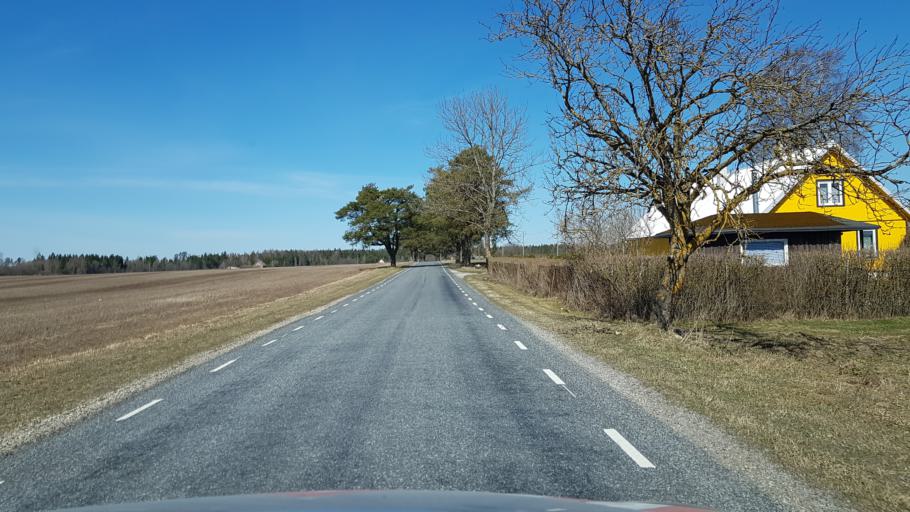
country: EE
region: Laeaene-Virumaa
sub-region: Vinni vald
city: Vinni
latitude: 59.1141
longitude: 26.5238
